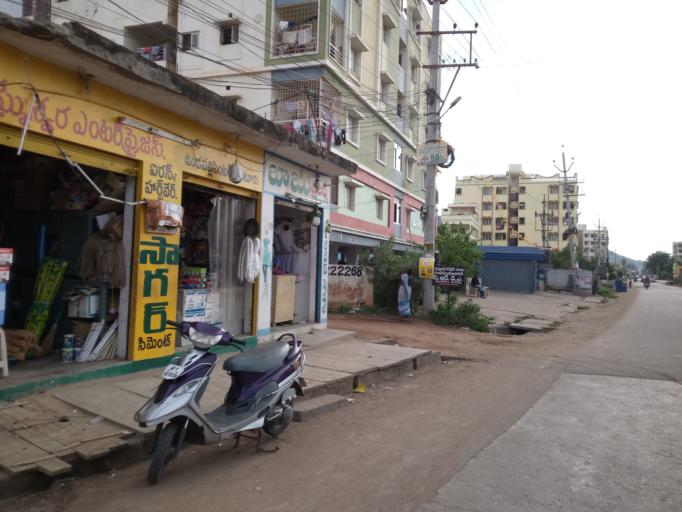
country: IN
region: Andhra Pradesh
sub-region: Guntur
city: Tadepalle
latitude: 16.4924
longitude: 80.5978
